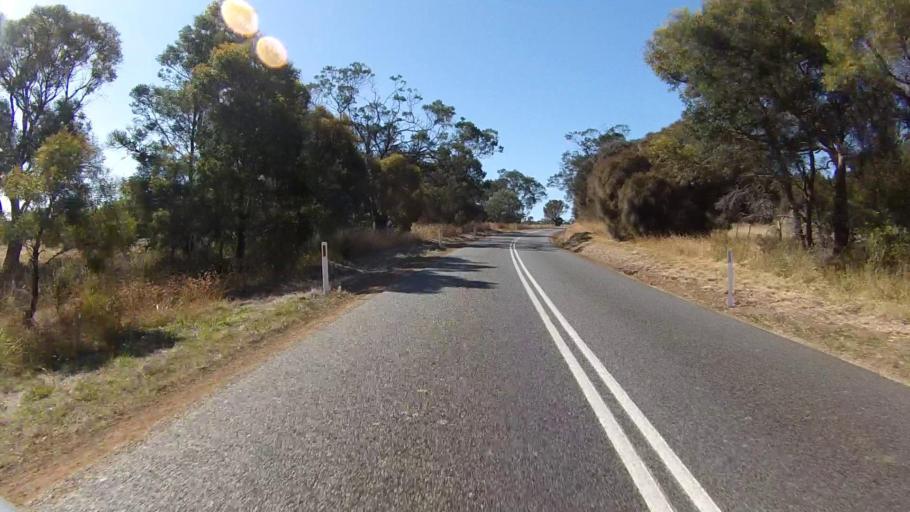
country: AU
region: Tasmania
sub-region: Sorell
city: Sorell
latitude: -42.2928
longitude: 147.9896
